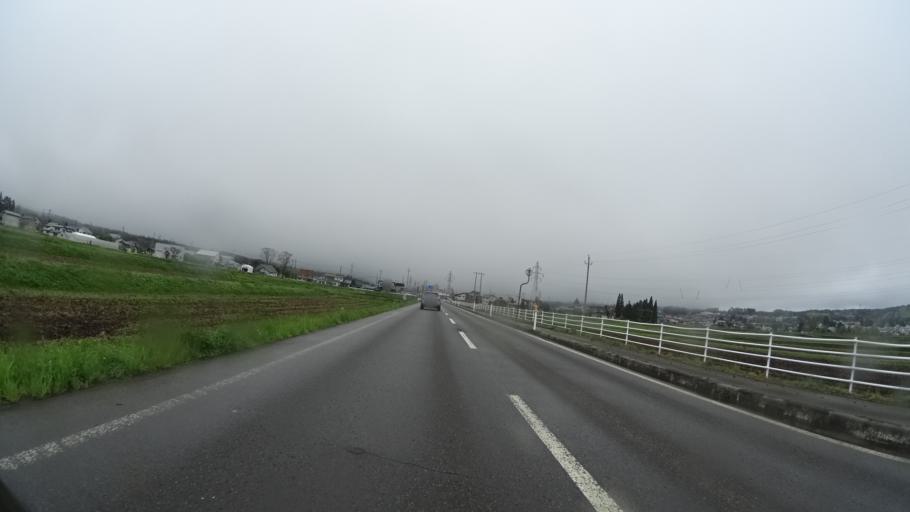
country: JP
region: Nagano
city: Nagano-shi
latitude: 36.7992
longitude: 138.1950
